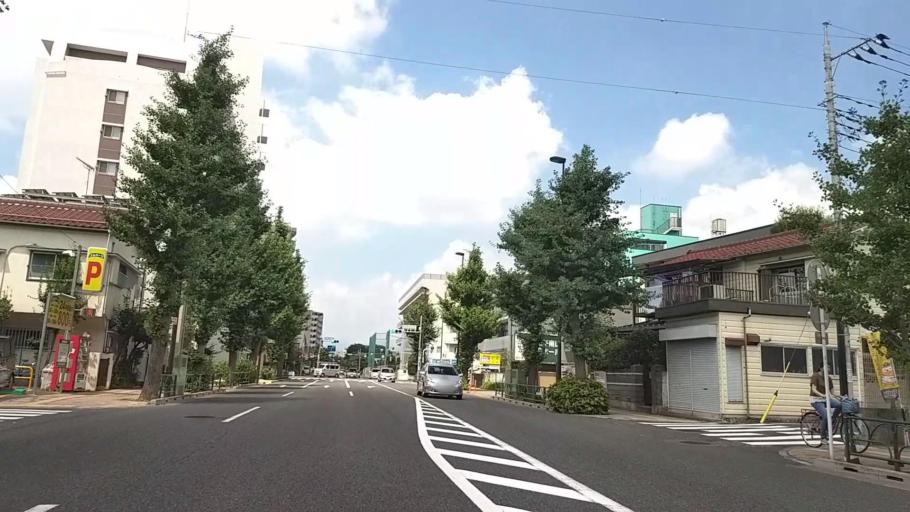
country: JP
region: Tokyo
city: Hachioji
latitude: 35.6546
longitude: 139.3338
